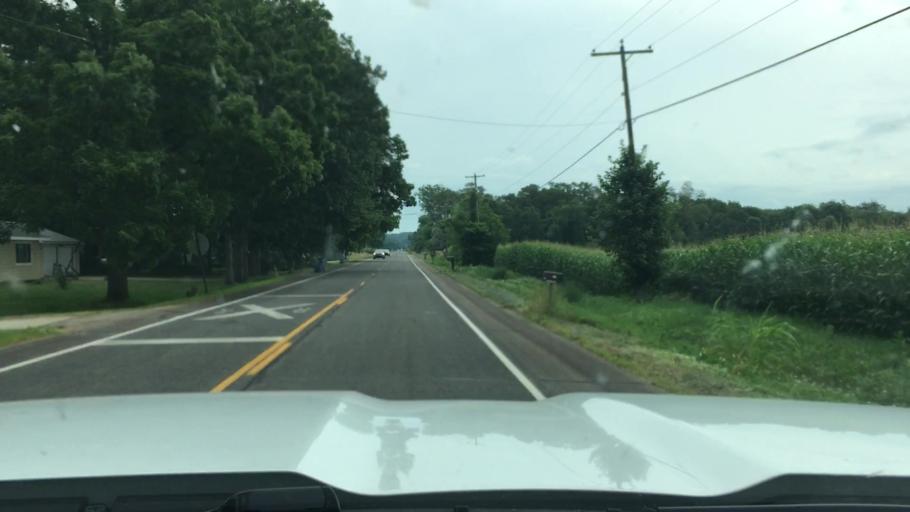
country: US
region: Michigan
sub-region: Allegan County
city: Plainwell
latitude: 42.4646
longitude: -85.6301
